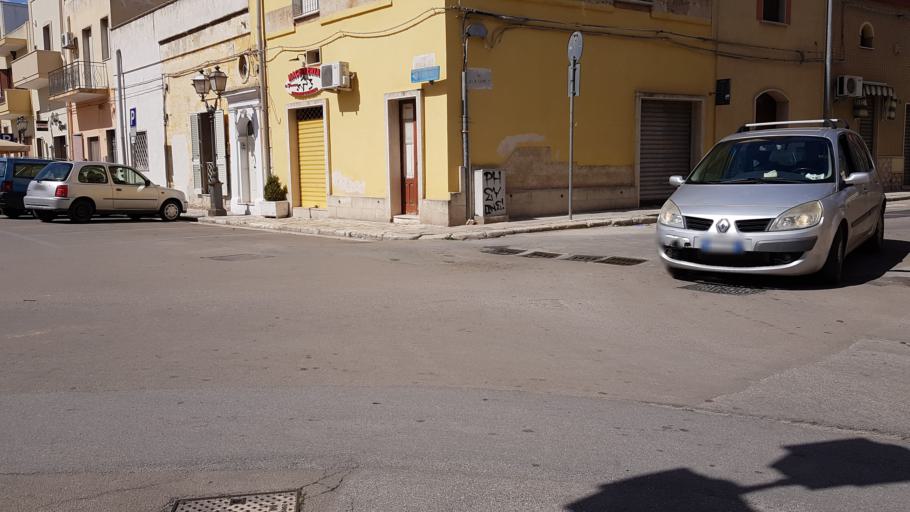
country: IT
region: Apulia
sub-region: Provincia di Brindisi
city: Mesagne
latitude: 40.5557
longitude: 17.8125
